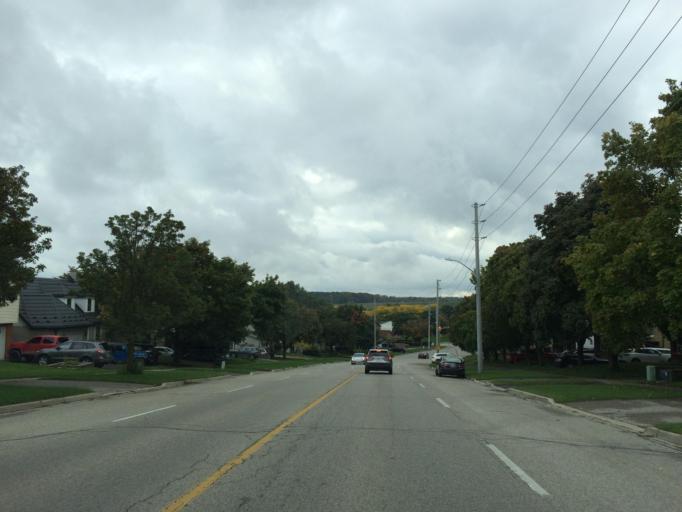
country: CA
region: Ontario
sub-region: Wellington County
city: Guelph
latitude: 43.5303
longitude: -80.2911
